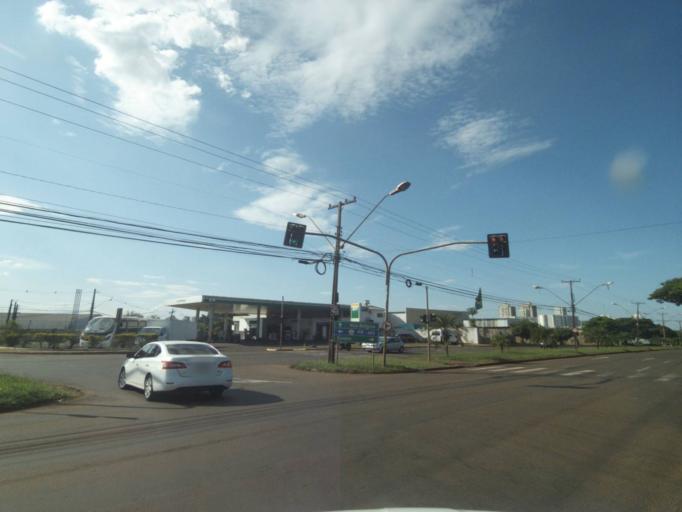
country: BR
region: Parana
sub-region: Londrina
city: Londrina
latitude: -23.3573
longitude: -51.1501
